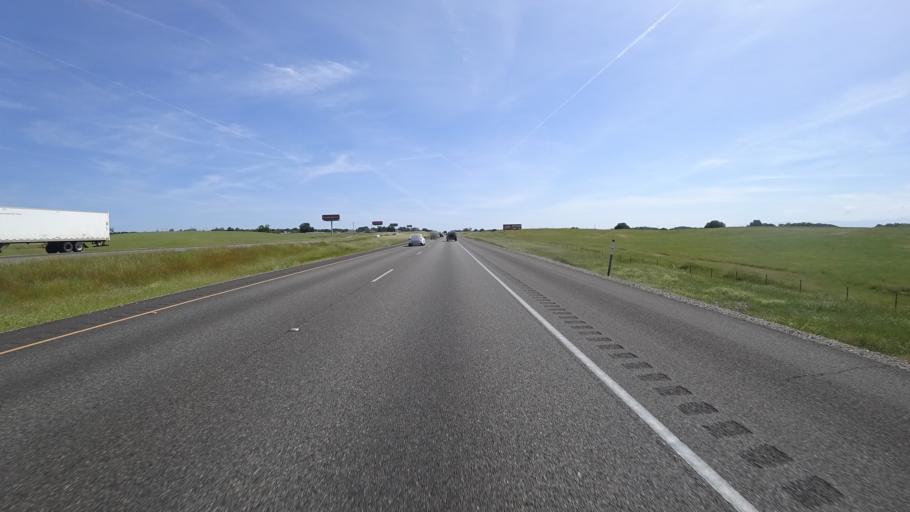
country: US
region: California
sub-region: Shasta County
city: Cottonwood
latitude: 40.3126
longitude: -122.2805
